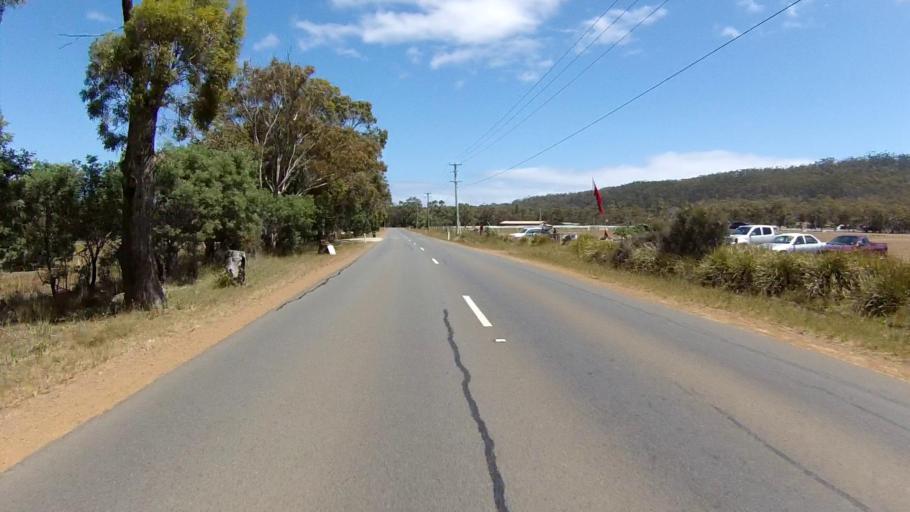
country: AU
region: Tasmania
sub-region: Clarence
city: Sandford
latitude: -42.9436
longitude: 147.4849
